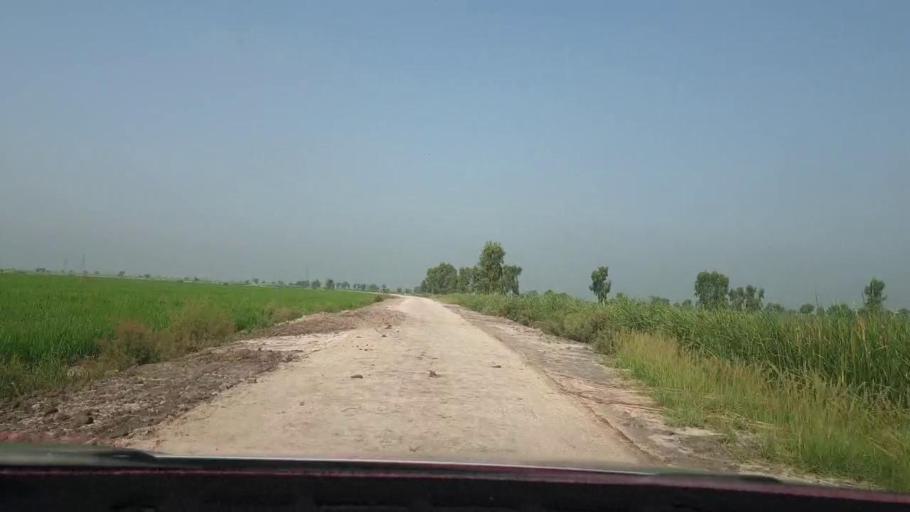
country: PK
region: Sindh
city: Nasirabad
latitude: 27.4312
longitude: 67.9537
